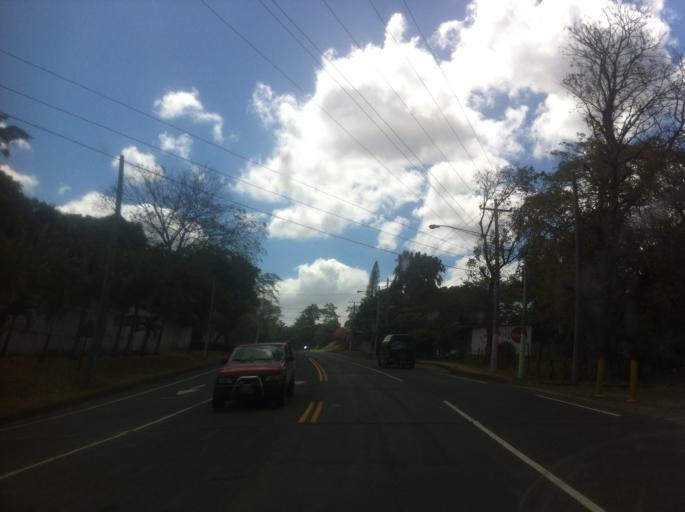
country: NI
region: Managua
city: El Crucero
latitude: 12.0682
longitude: -86.3240
